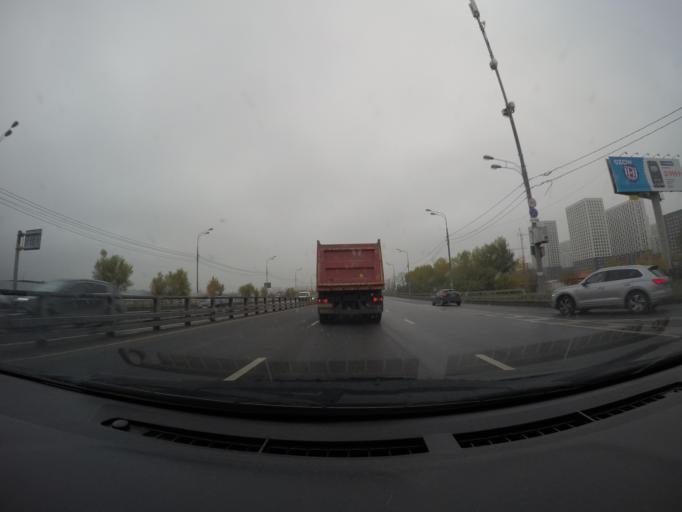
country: RU
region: Moskovskaya
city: Shcherbinka
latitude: 55.5220
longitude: 37.5781
